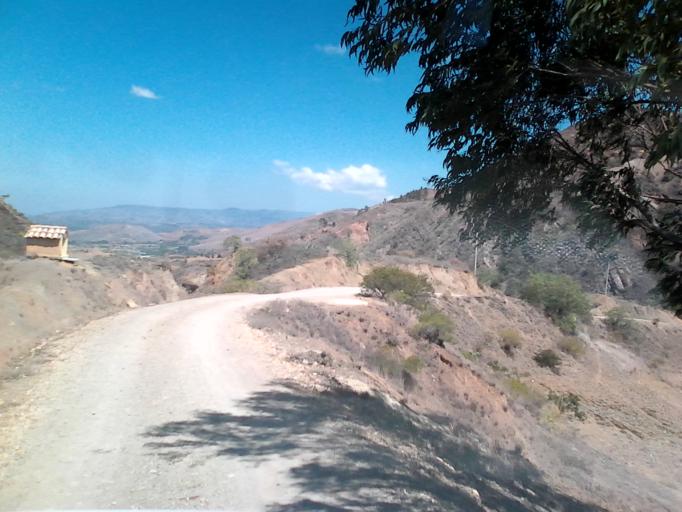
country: CO
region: Boyaca
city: Sachica
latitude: 5.5485
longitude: -73.5315
